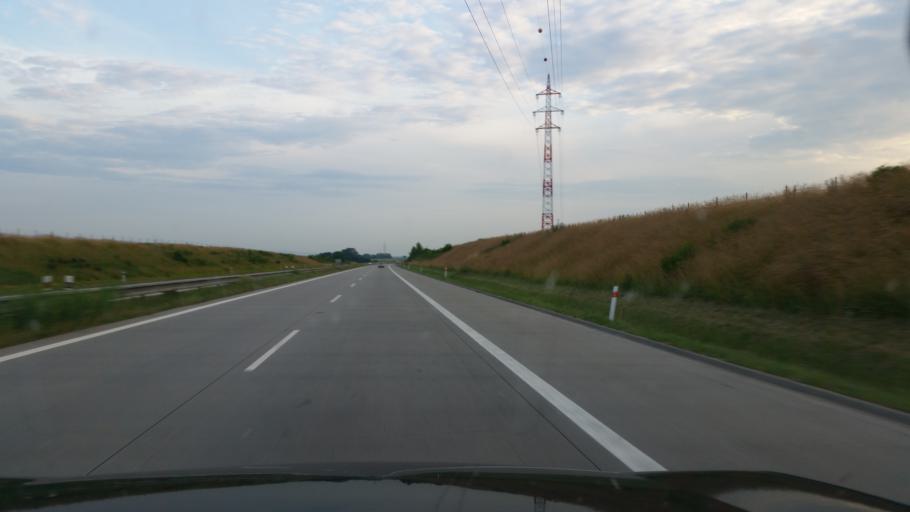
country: CZ
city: Bilovec
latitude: 49.7190
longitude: 18.0069
